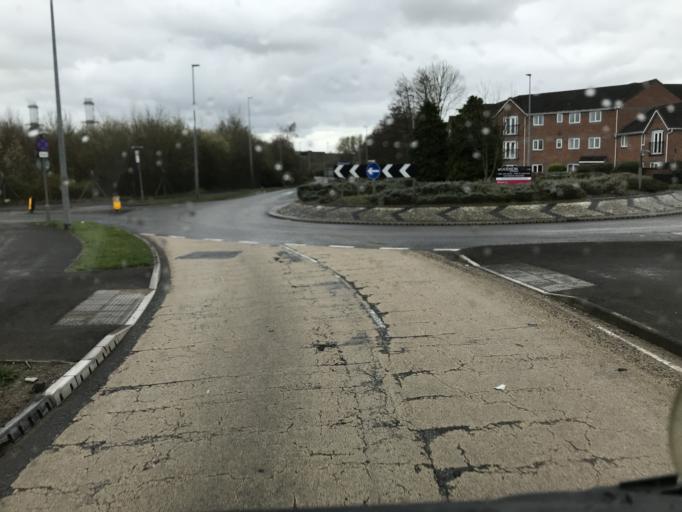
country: GB
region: England
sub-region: City and Borough of Salford
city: Irlam
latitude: 53.4430
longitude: -2.4122
